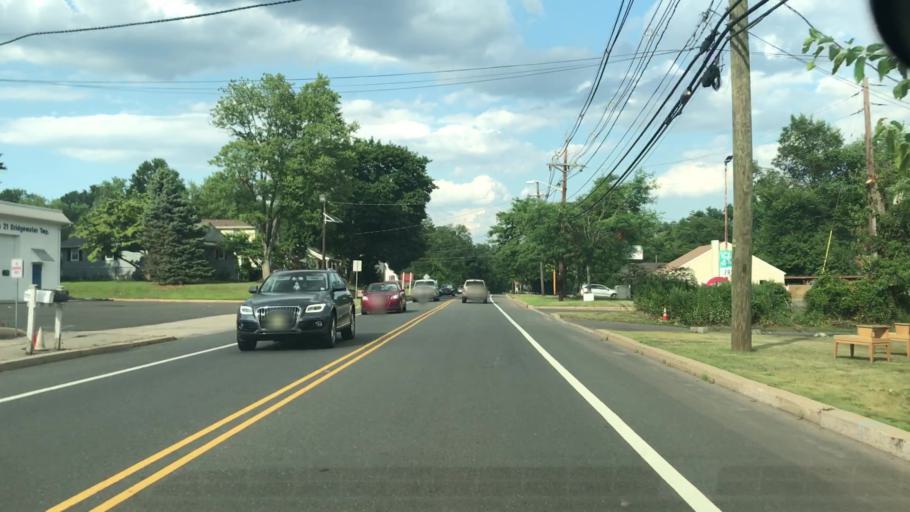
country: US
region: New Jersey
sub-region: Somerset County
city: Bradley Gardens
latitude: 40.5600
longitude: -74.6512
